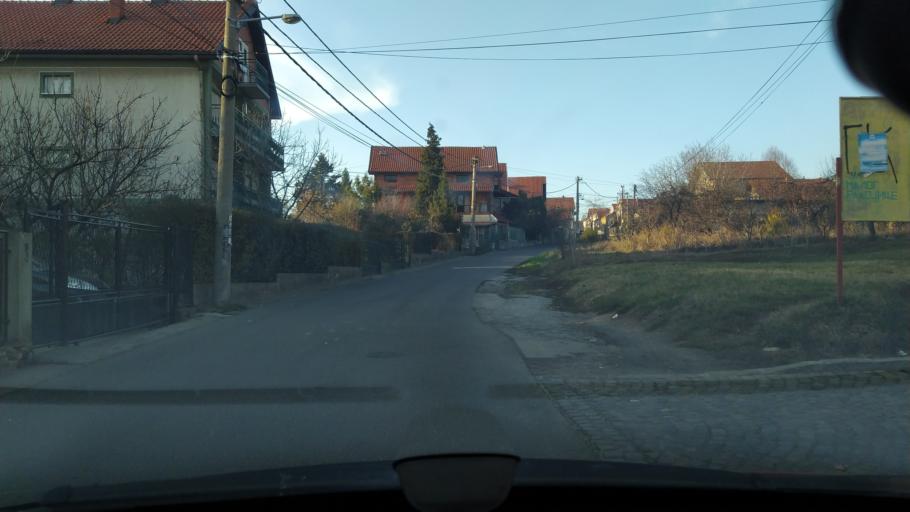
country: RS
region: Central Serbia
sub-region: Belgrade
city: Zvezdara
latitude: 44.7569
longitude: 20.5676
